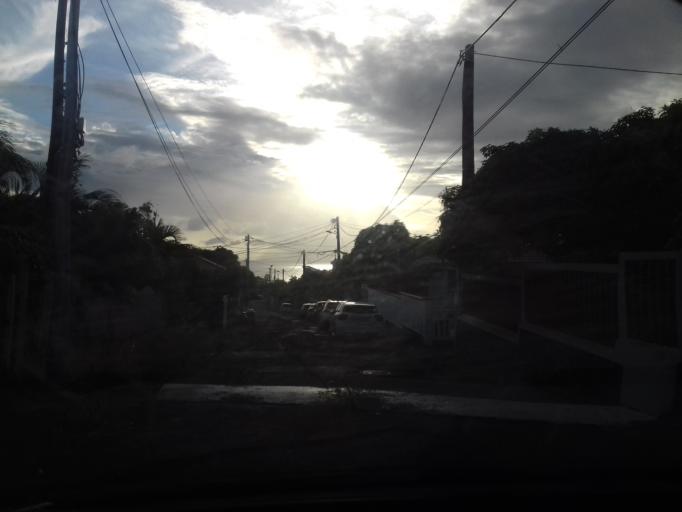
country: MQ
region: Martinique
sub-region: Martinique
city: Fort-de-France
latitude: 14.6157
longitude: -61.0914
